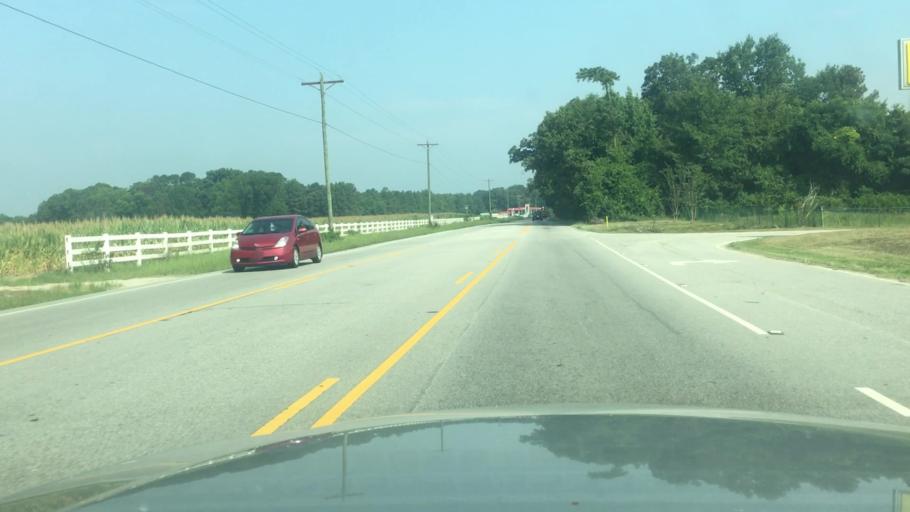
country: US
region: North Carolina
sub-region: Cumberland County
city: Hope Mills
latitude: 34.9311
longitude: -78.9161
